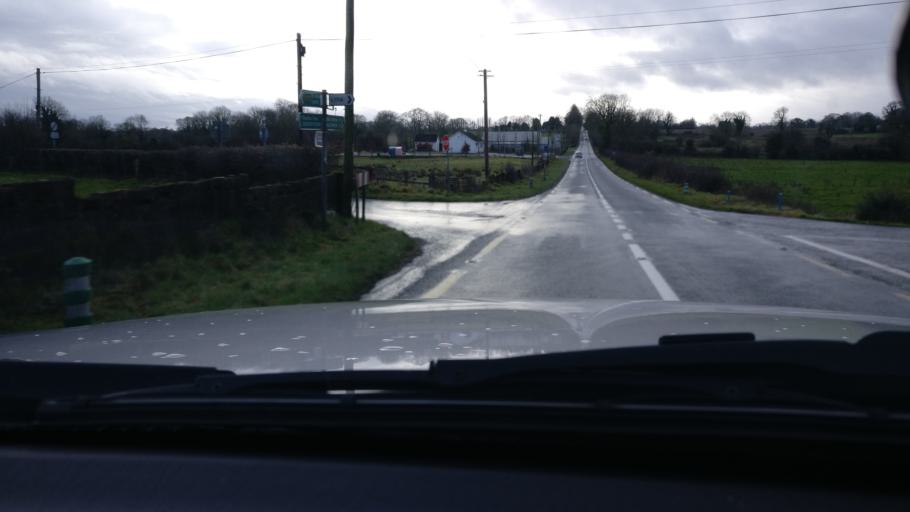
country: IE
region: Leinster
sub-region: An Iarmhi
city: Moate
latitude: 53.6101
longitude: -7.7085
